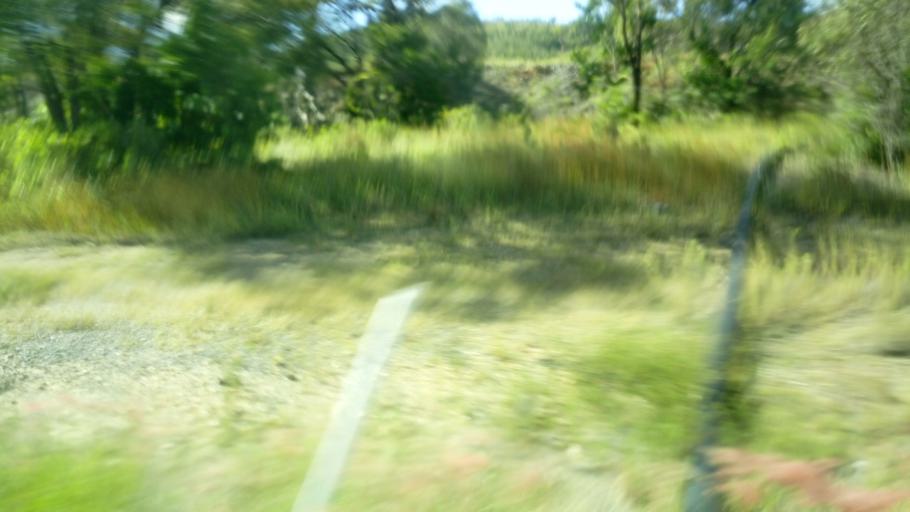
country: AU
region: Queensland
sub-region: Cairns
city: Port Douglas
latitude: -16.5275
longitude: 145.1285
